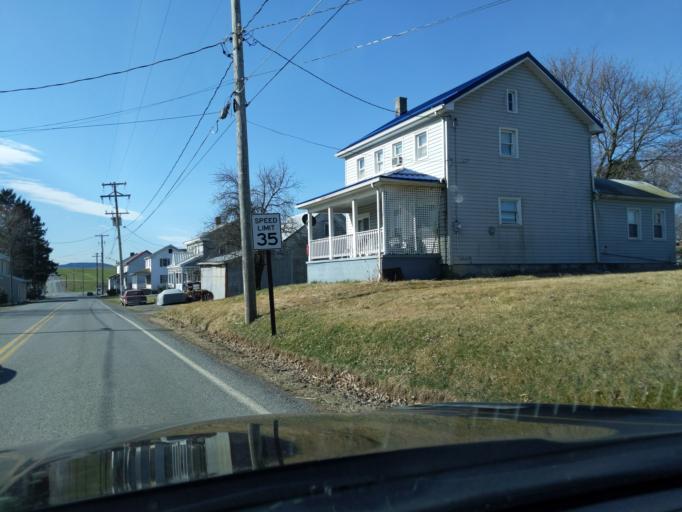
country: US
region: Pennsylvania
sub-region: Blair County
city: Martinsburg
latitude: 40.3085
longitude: -78.2815
